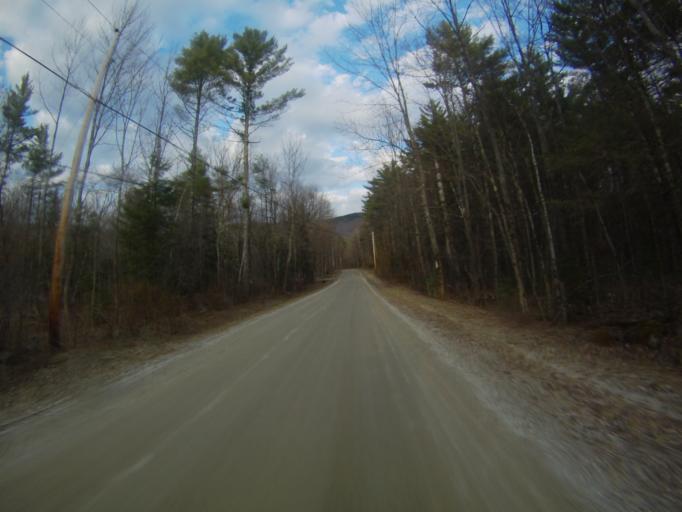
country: US
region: Vermont
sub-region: Rutland County
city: Brandon
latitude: 43.8552
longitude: -73.0036
